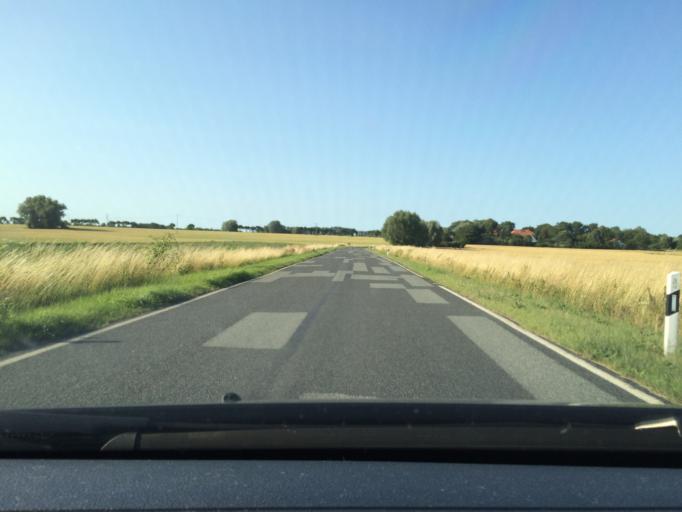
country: DE
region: Mecklenburg-Vorpommern
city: Altenpleen
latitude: 54.3810
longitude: 12.9422
